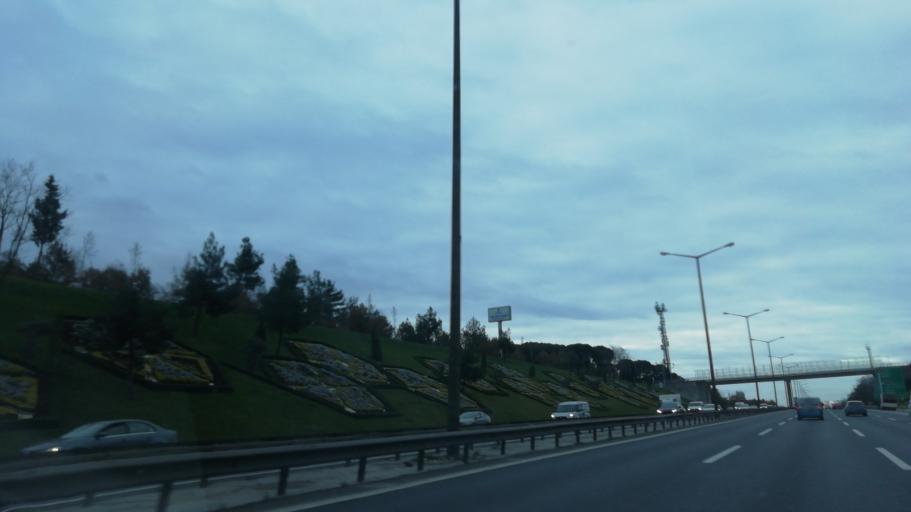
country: TR
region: Istanbul
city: Umraniye
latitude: 41.0678
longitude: 29.1087
